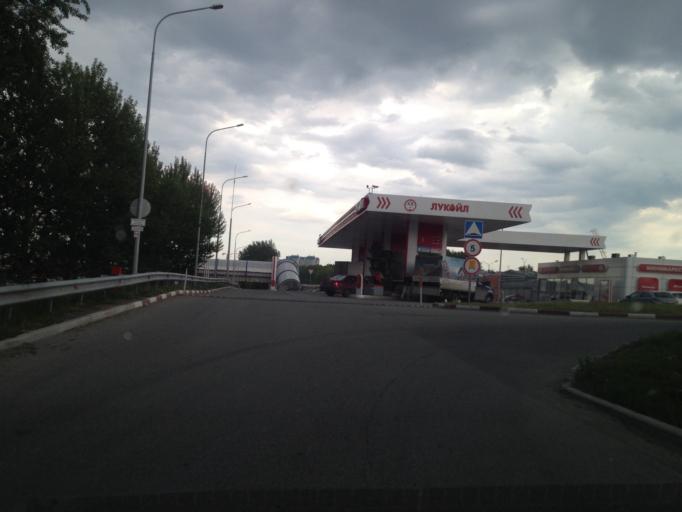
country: RU
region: Sverdlovsk
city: Yekaterinburg
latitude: 56.7890
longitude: 60.6157
